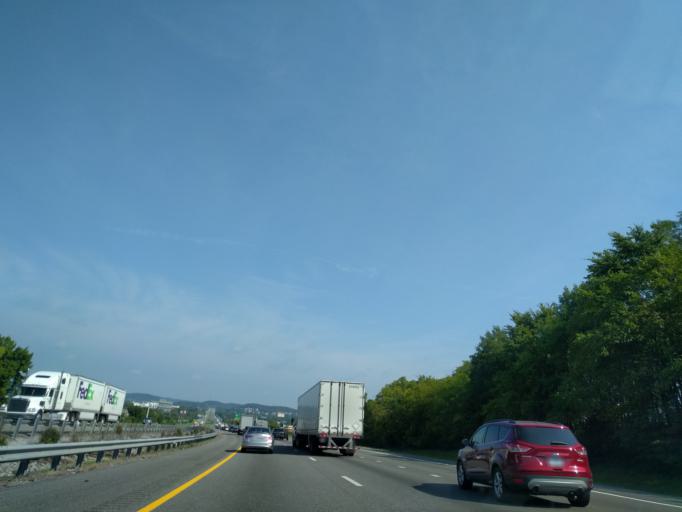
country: US
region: Tennessee
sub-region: Davidson County
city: Goodlettsville
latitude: 36.3164
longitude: -86.7014
